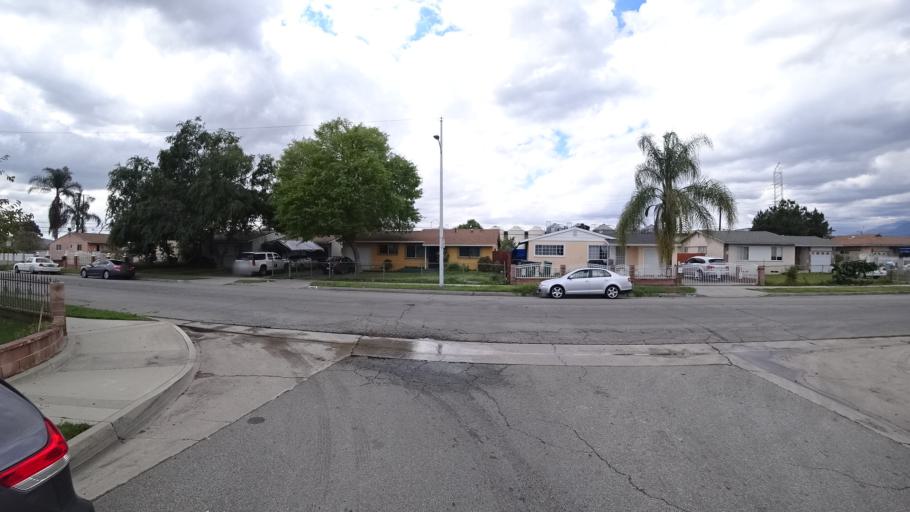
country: US
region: California
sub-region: Los Angeles County
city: Baldwin Park
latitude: 34.0928
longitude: -117.9818
